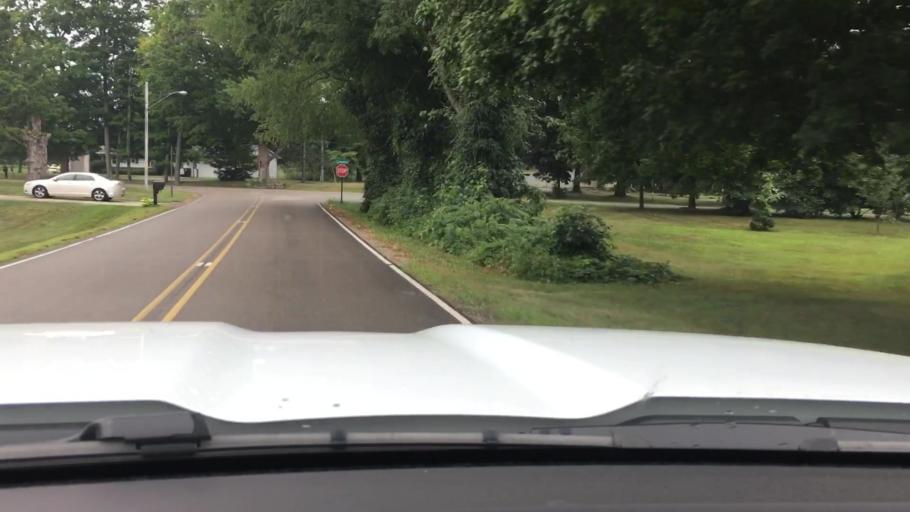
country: US
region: Michigan
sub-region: Kent County
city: Byron Center
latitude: 42.8438
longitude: -85.7421
